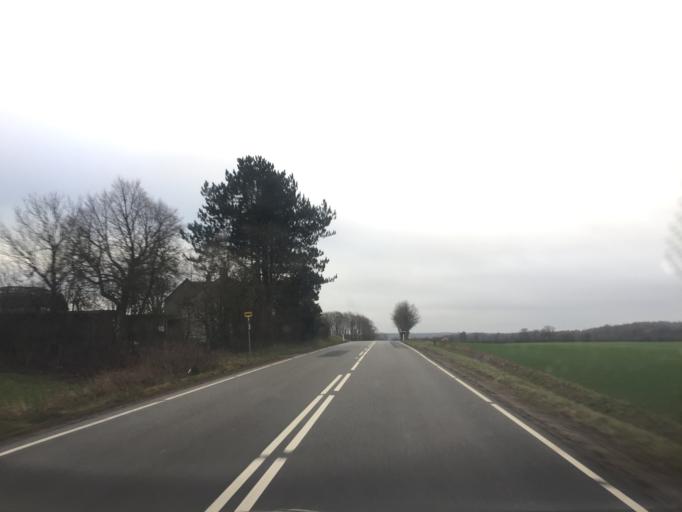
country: DK
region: South Denmark
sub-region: Svendborg Kommune
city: Thuro By
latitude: 55.1833
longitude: 10.6728
